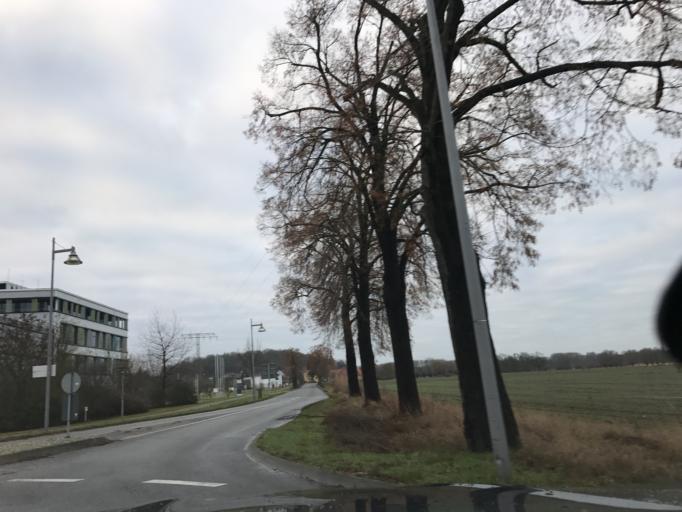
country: DE
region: Brandenburg
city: Werder
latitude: 52.4143
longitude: 12.9666
